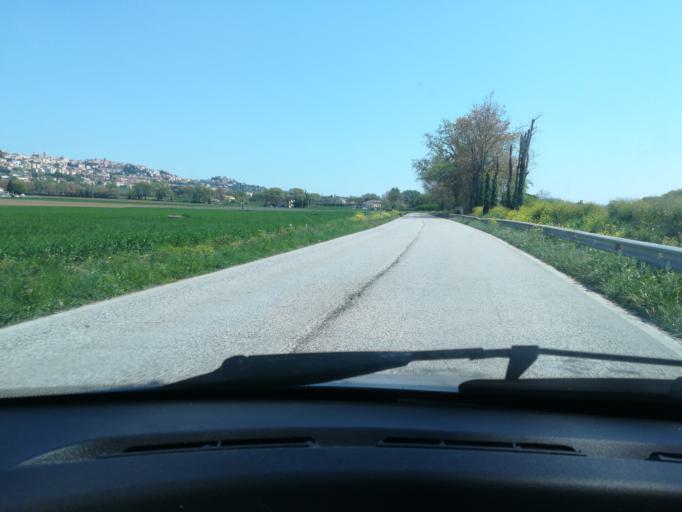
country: IT
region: The Marches
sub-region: Provincia di Ancona
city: Campocavallo
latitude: 43.4552
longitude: 13.5203
